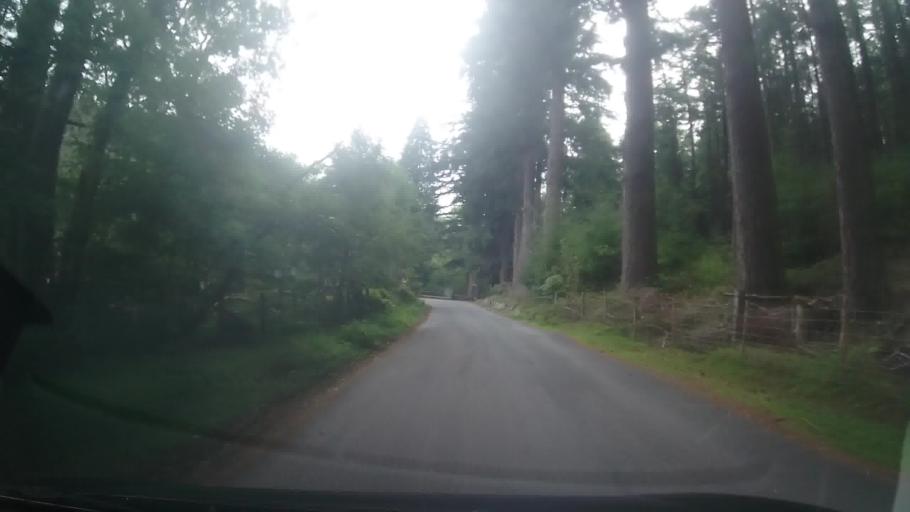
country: GB
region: Wales
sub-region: Sir Powys
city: Rhayader
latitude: 52.2937
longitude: -3.5901
